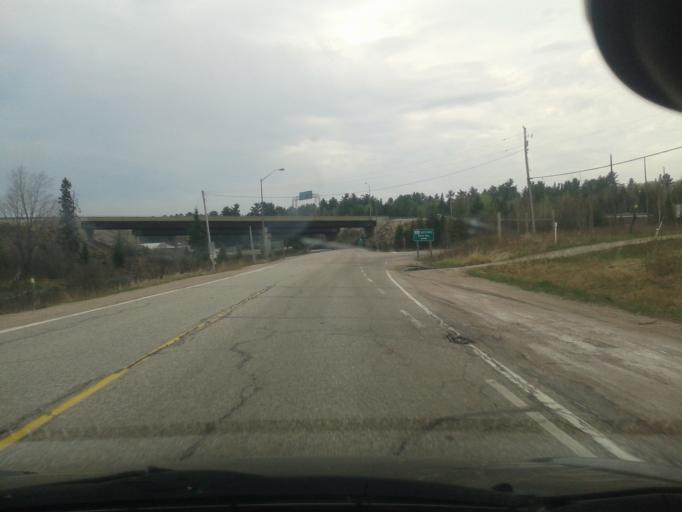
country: CA
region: Ontario
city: Powassan
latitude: 46.1949
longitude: -79.3538
